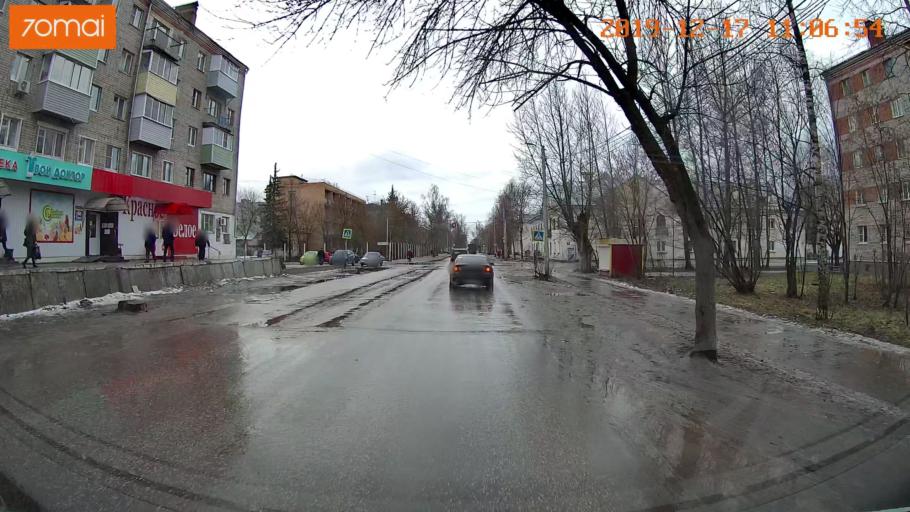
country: RU
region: Vladimir
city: Gus'-Khrustal'nyy
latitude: 55.6135
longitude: 40.6446
